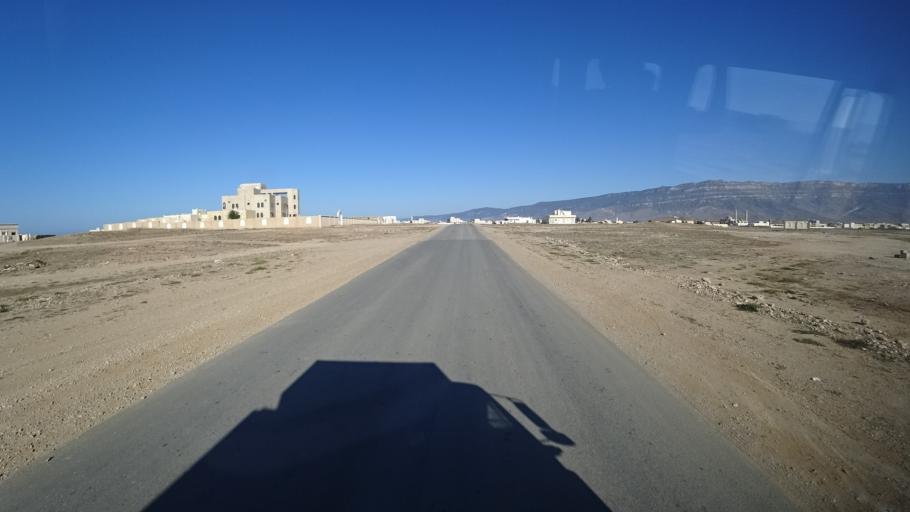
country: OM
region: Zufar
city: Salalah
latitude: 16.9794
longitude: 54.6987
